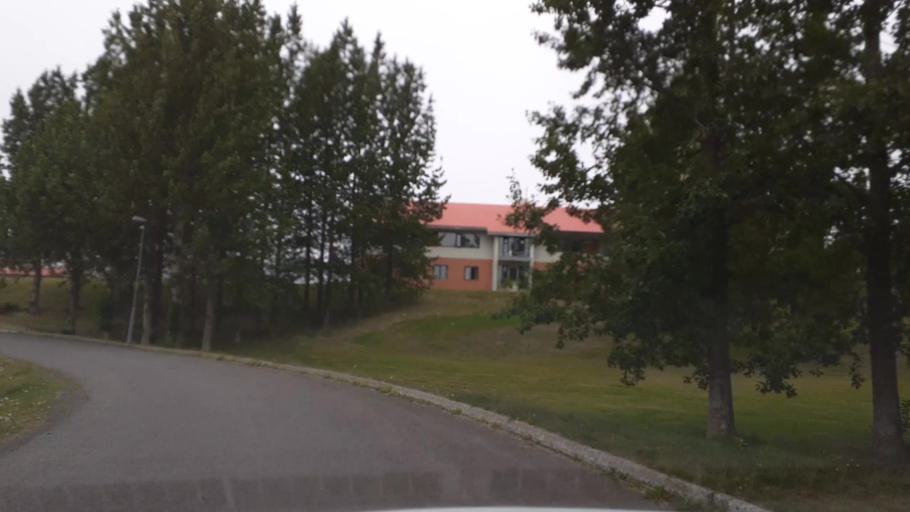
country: IS
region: Northeast
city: Siglufjoerdur
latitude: 65.7322
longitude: -19.1106
